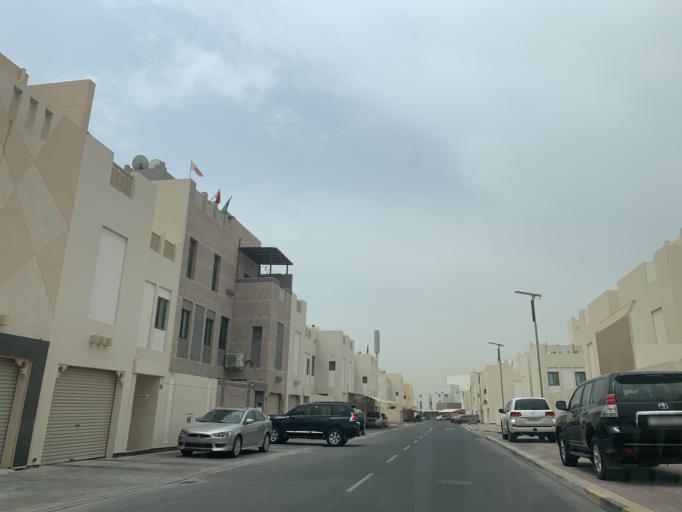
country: BH
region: Northern
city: Madinat `Isa
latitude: 26.1761
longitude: 50.5158
